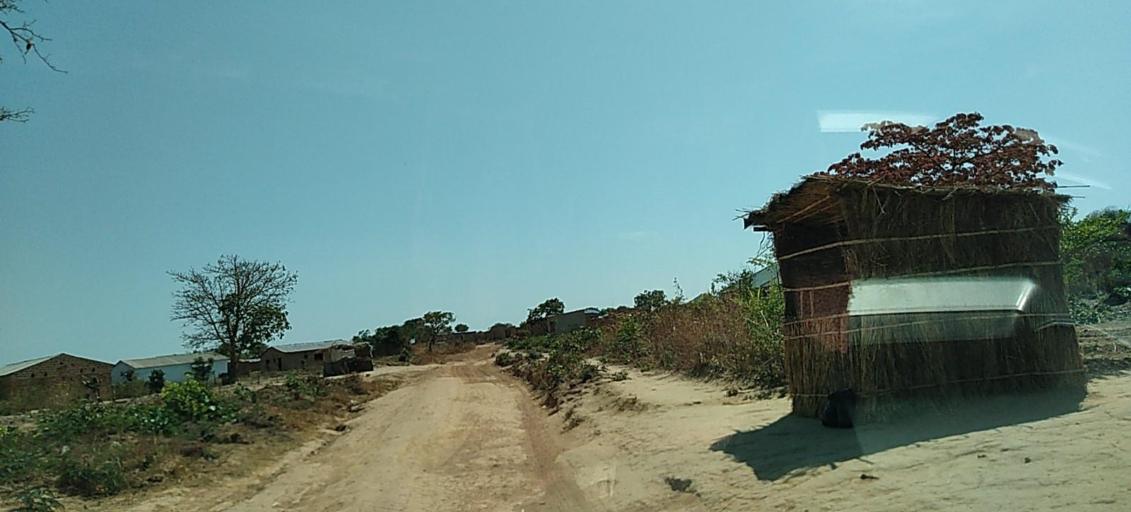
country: ZM
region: Copperbelt
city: Chililabombwe
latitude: -12.3204
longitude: 27.8609
